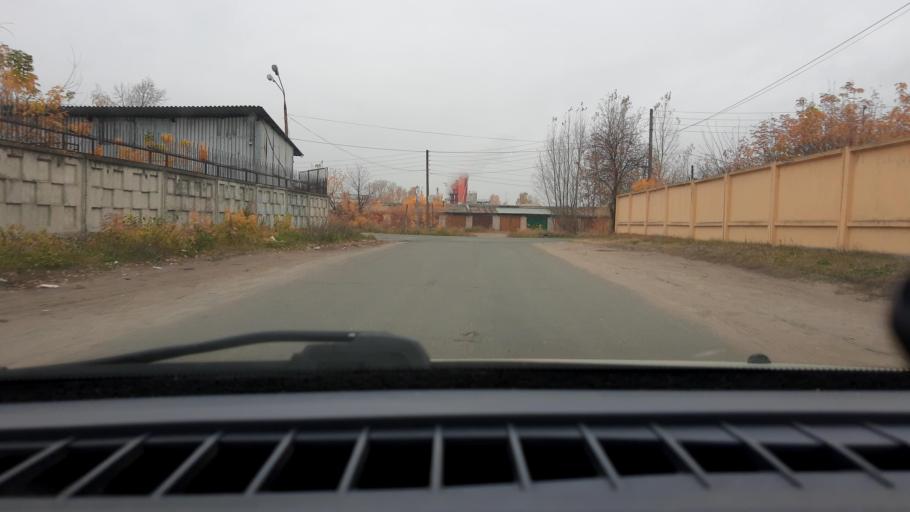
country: RU
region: Nizjnij Novgorod
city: Gorbatovka
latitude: 56.3363
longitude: 43.8074
